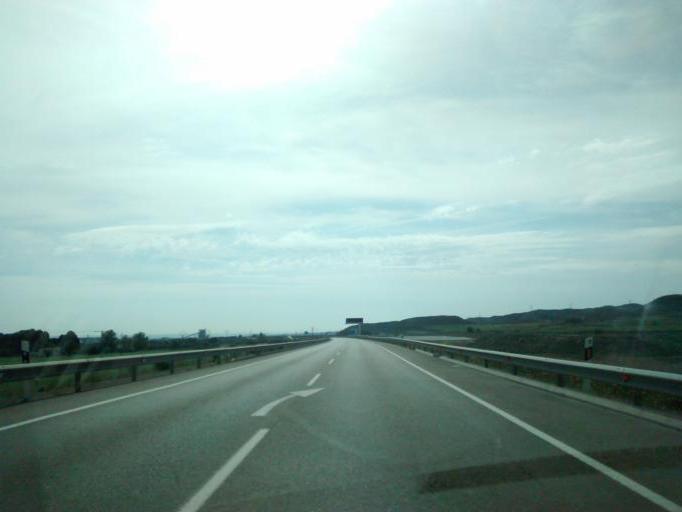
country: ES
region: Aragon
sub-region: Provincia de Zaragoza
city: El Burgo de Ebro
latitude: 41.5514
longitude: -0.7116
